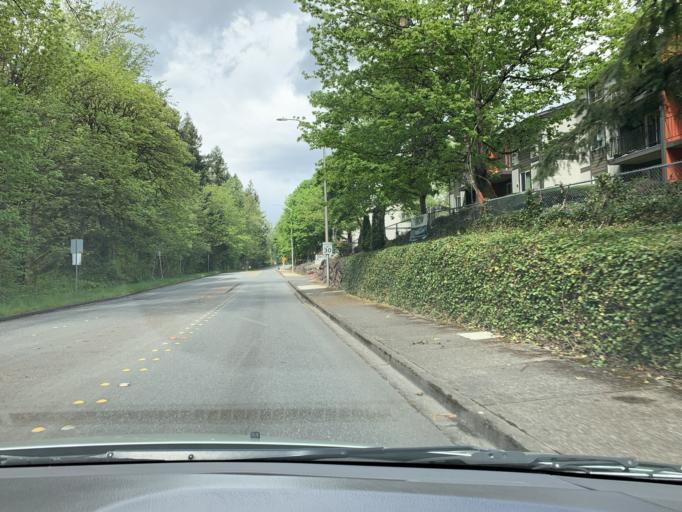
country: US
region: Washington
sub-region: King County
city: Kent
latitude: 47.3720
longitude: -122.2094
